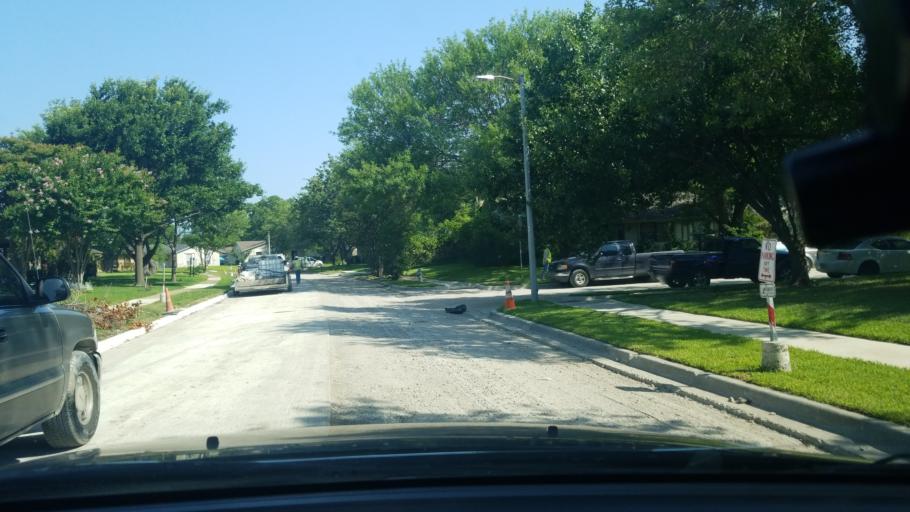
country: US
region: Texas
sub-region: Dallas County
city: Mesquite
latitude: 32.8168
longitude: -96.6459
